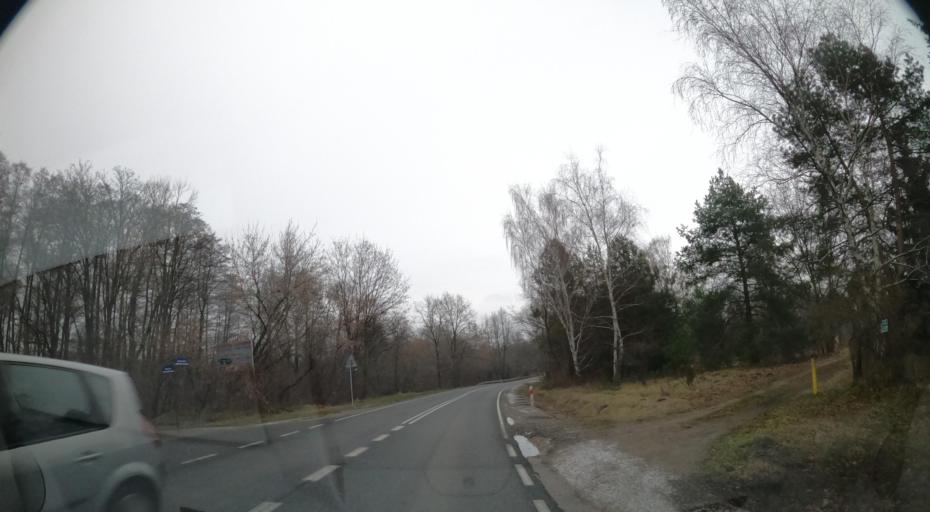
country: PL
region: Masovian Voivodeship
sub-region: Powiat radomski
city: Jastrzebia
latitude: 51.4321
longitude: 21.2436
